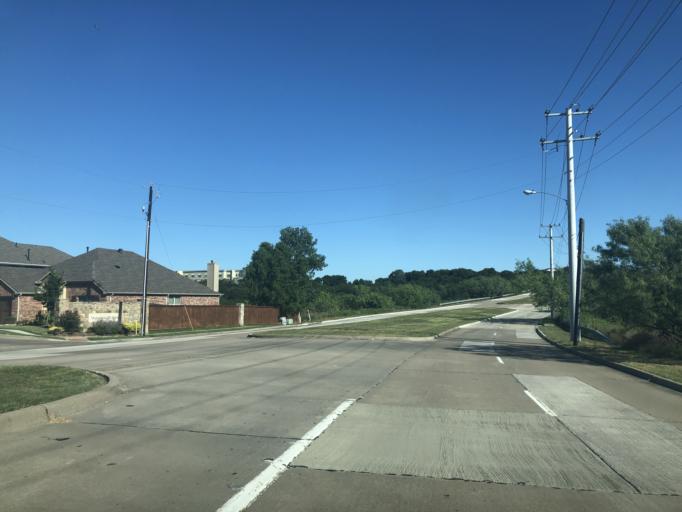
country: US
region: Texas
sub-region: Dallas County
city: Duncanville
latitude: 32.6591
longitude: -96.9629
